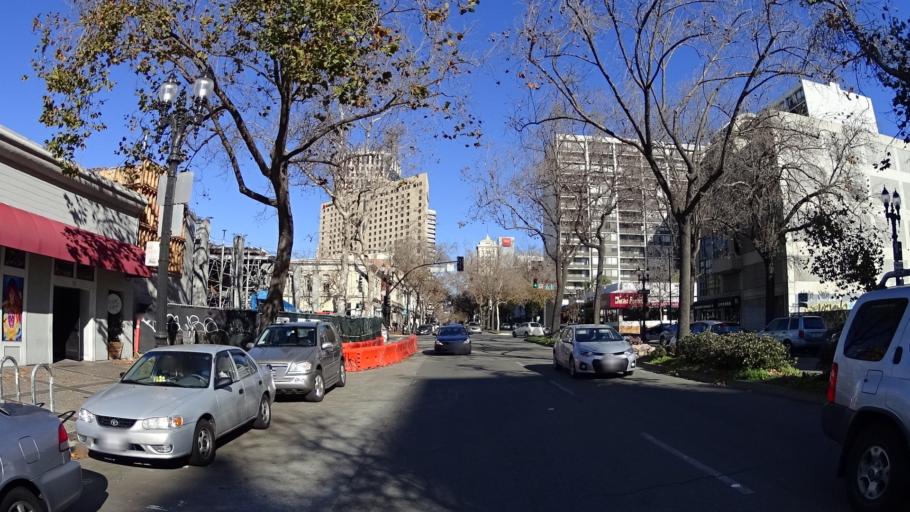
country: US
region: California
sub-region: Alameda County
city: Oakland
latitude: 37.7998
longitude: -122.2741
